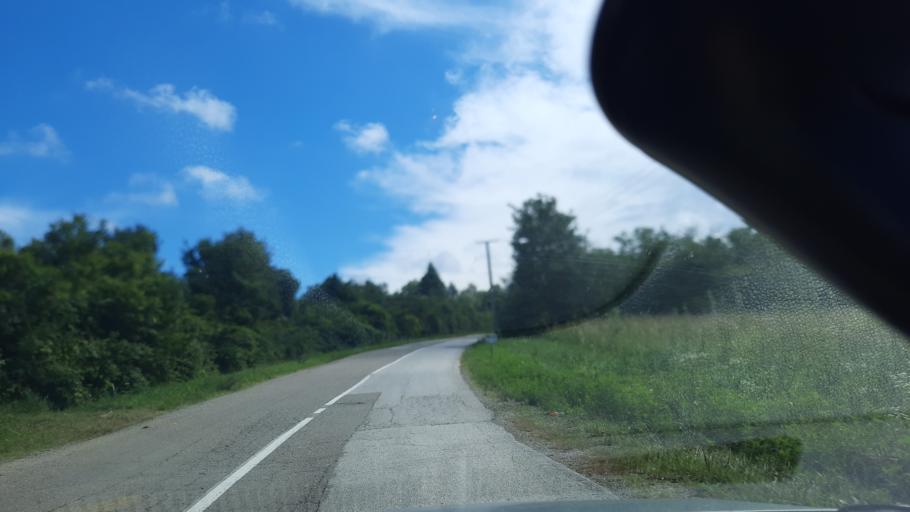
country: RS
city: Glozan
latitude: 45.1666
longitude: 19.5883
